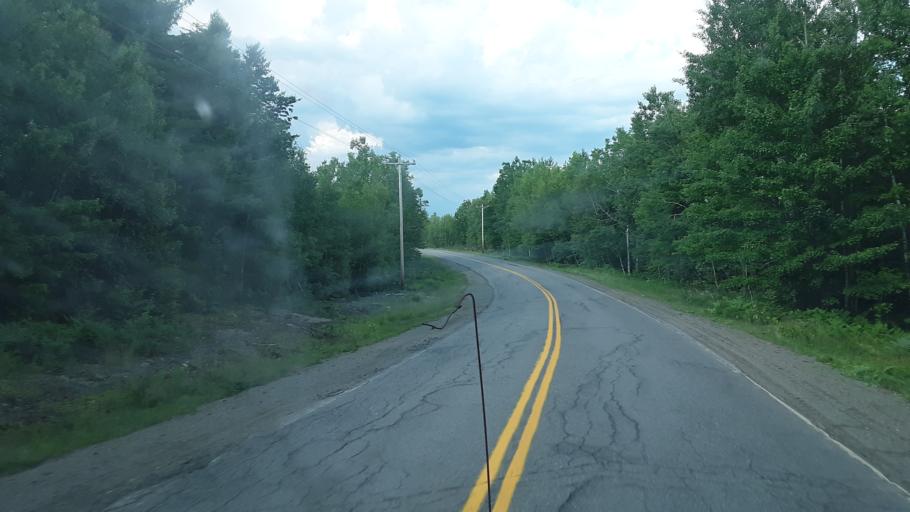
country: US
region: Maine
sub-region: Washington County
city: Calais
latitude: 45.1189
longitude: -67.5009
